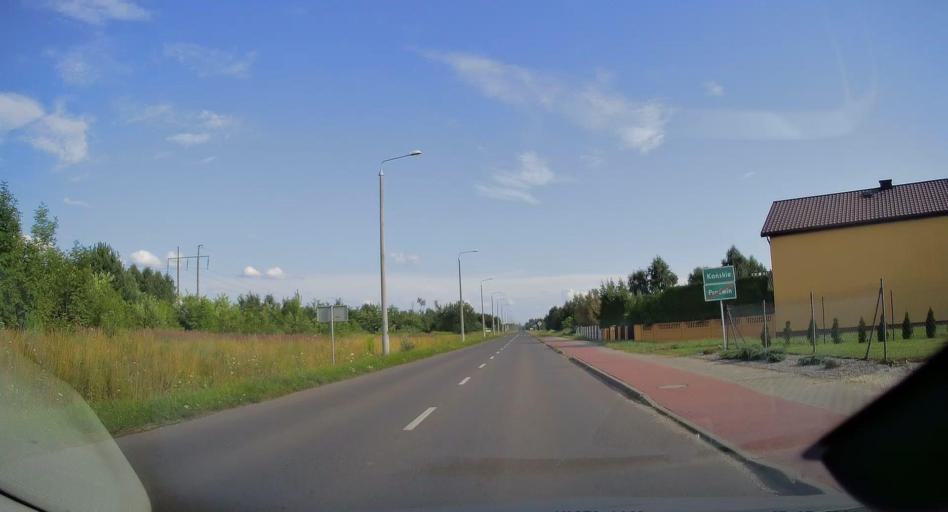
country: PL
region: Swietokrzyskie
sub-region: Powiat konecki
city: Konskie
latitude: 51.2147
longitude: 20.3925
